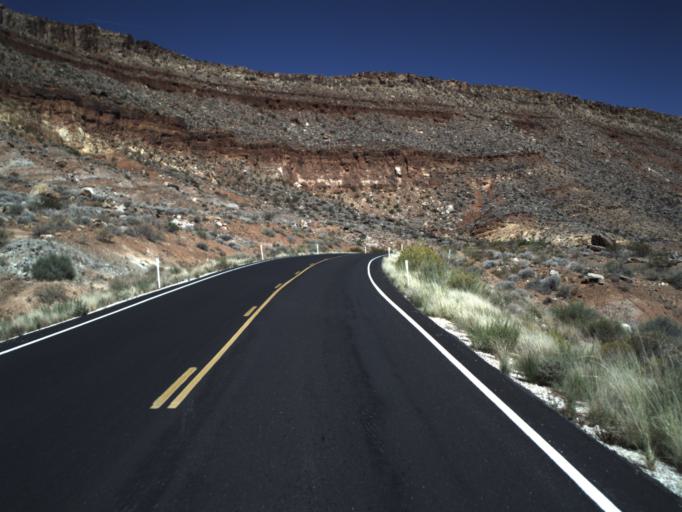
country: US
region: Utah
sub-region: Washington County
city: Hurricane
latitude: 37.1827
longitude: -113.3974
